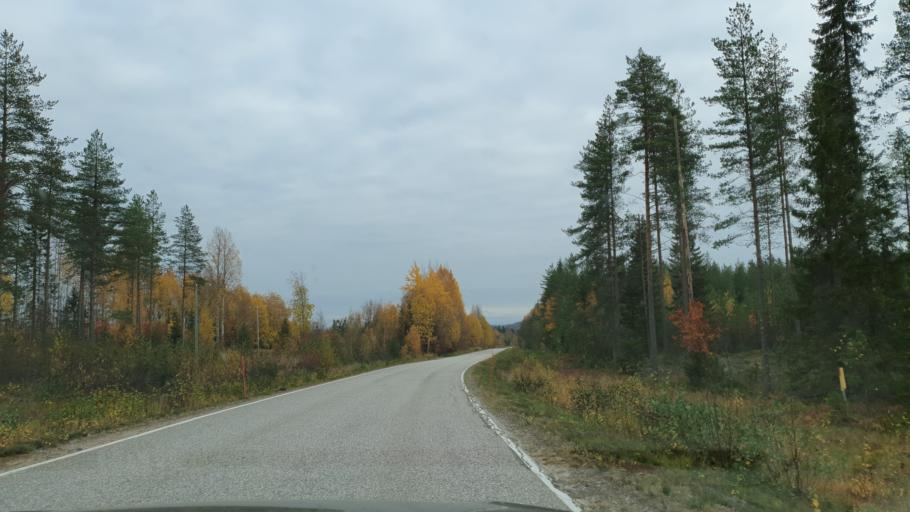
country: FI
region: Kainuu
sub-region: Kajaani
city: Ristijaervi
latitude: 64.4702
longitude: 28.2979
